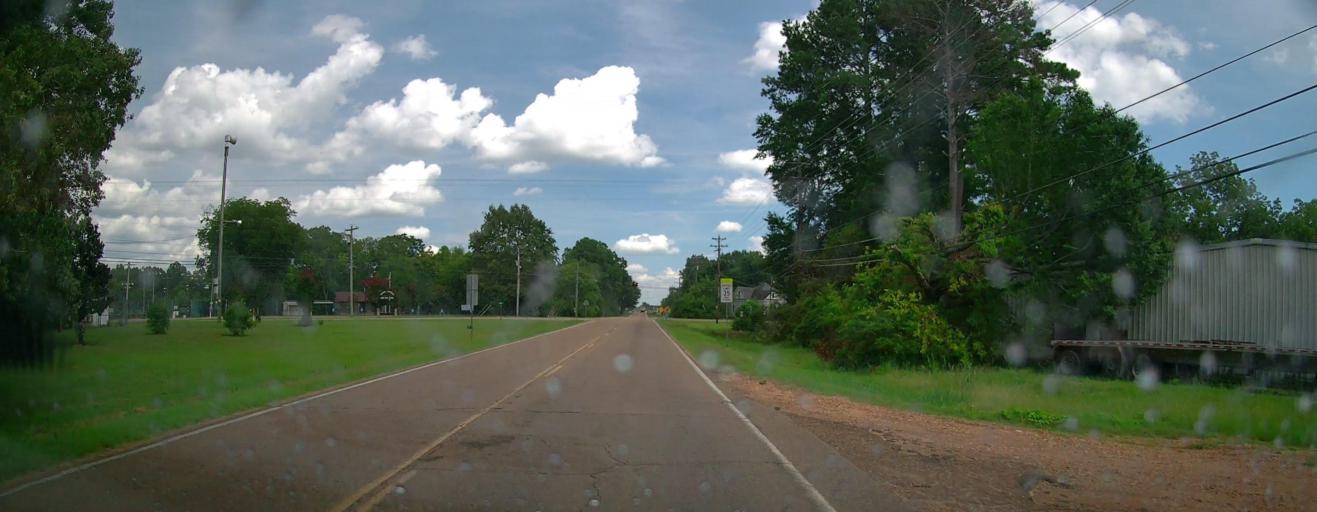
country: US
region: Mississippi
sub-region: Lee County
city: Shannon
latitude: 34.1226
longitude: -88.7153
